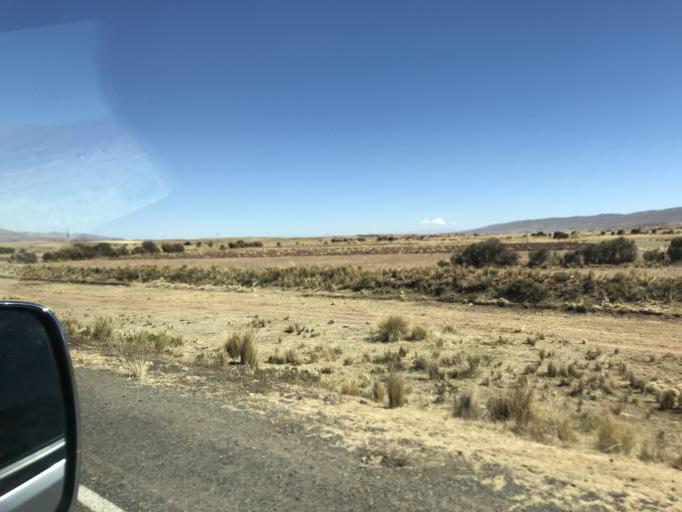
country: BO
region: La Paz
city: Tiahuanaco
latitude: -16.5924
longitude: -68.5706
